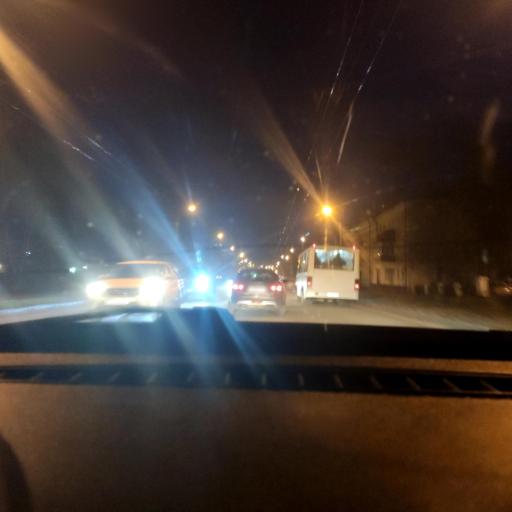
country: RU
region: Bashkortostan
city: Ufa
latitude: 54.7934
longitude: 56.1392
